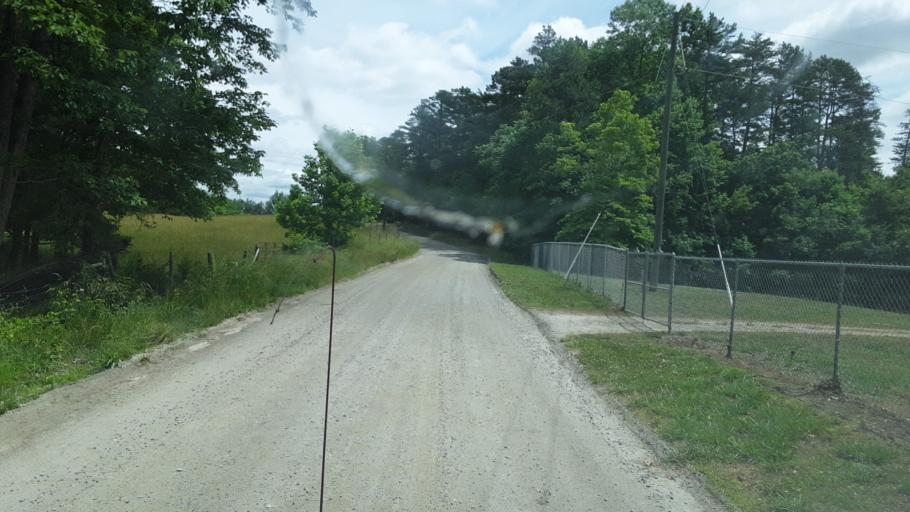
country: US
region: Virginia
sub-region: Pittsylvania County
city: Chatham
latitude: 36.8386
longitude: -79.4338
